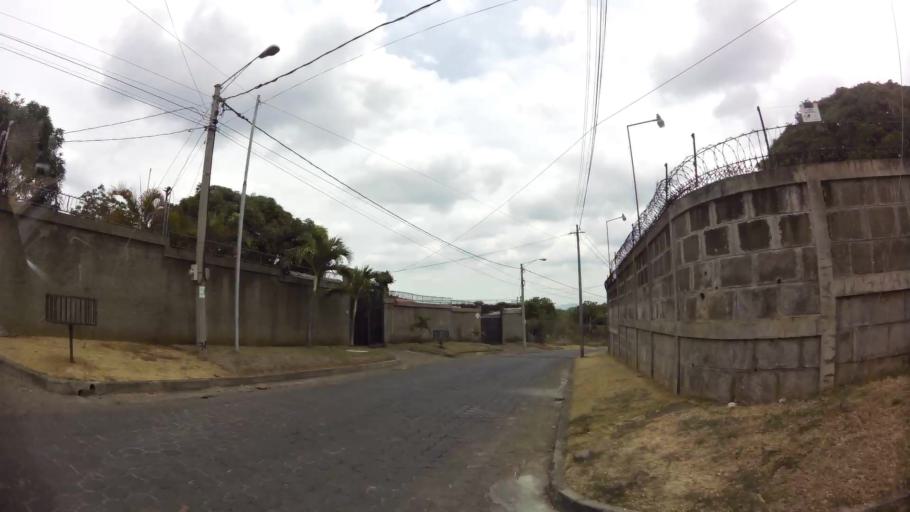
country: NI
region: Managua
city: Managua
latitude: 12.0951
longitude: -86.2255
